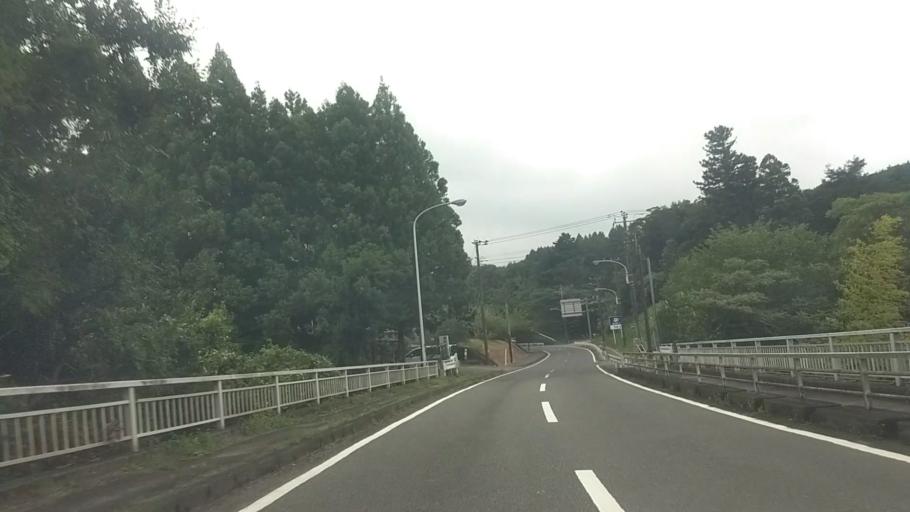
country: JP
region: Chiba
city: Kawaguchi
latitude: 35.2294
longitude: 140.0893
